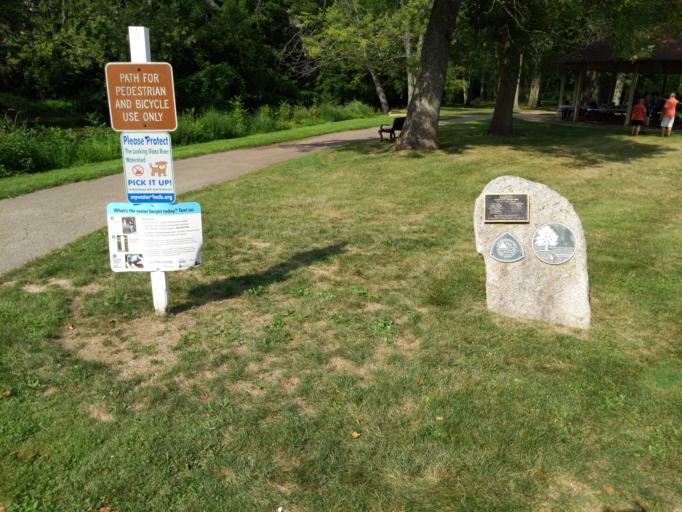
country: US
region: Michigan
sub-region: Clinton County
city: DeWitt
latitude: 42.8398
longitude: -84.5688
